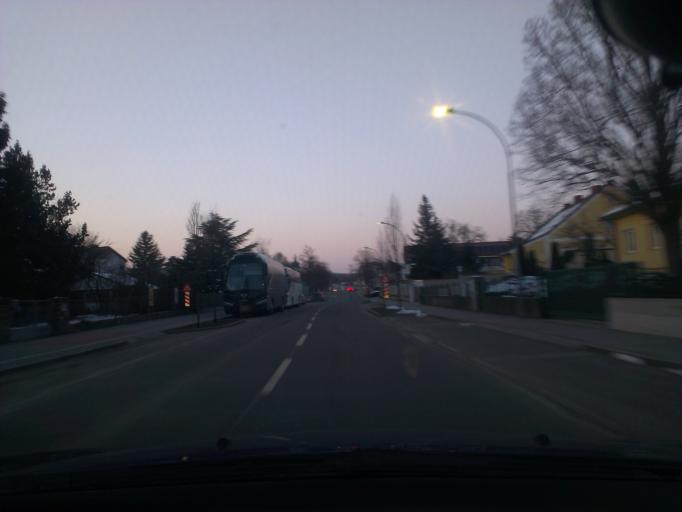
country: AT
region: Lower Austria
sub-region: Politischer Bezirk Wien-Umgebung
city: Fischamend Dorf
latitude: 48.1147
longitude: 16.6141
